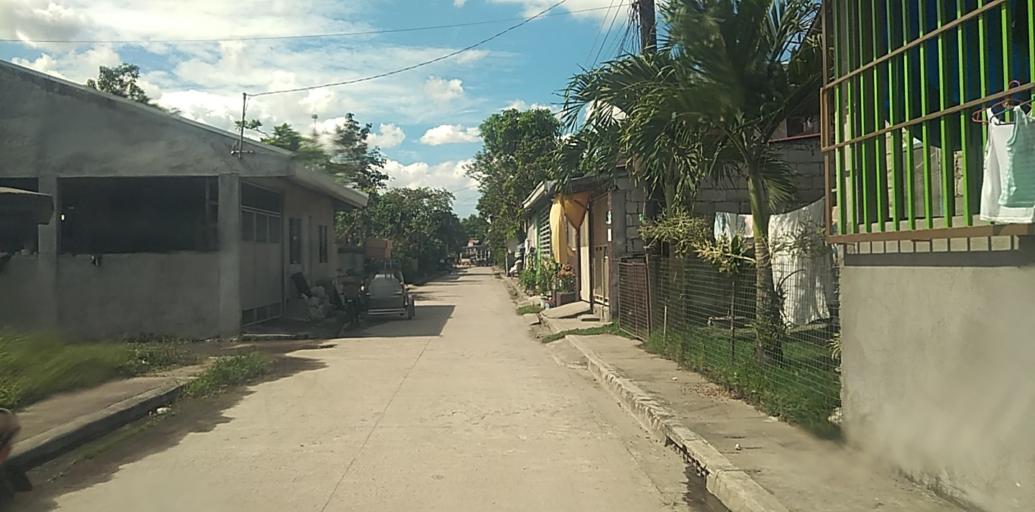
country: PH
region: Central Luzon
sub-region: Province of Pampanga
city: Buensuseso
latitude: 15.1922
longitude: 120.6646
